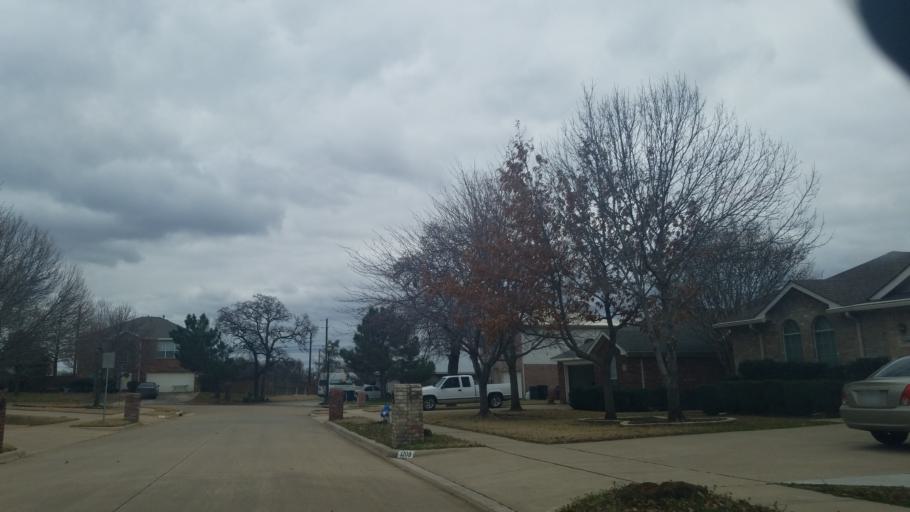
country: US
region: Texas
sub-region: Denton County
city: Corinth
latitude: 33.1332
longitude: -97.0890
